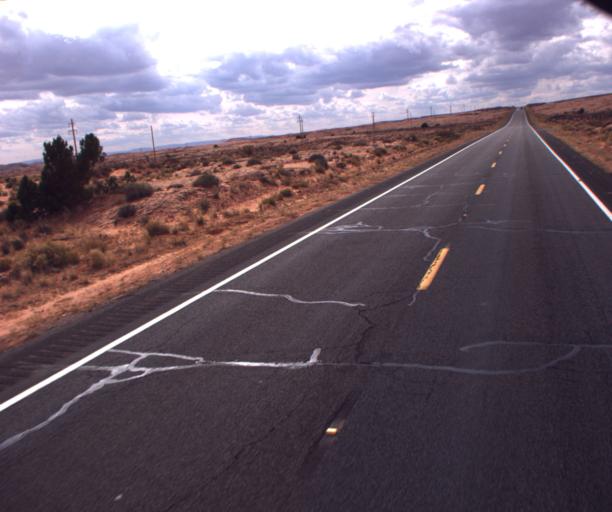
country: US
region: Arizona
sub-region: Navajo County
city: Kayenta
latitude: 36.9325
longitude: -109.7460
